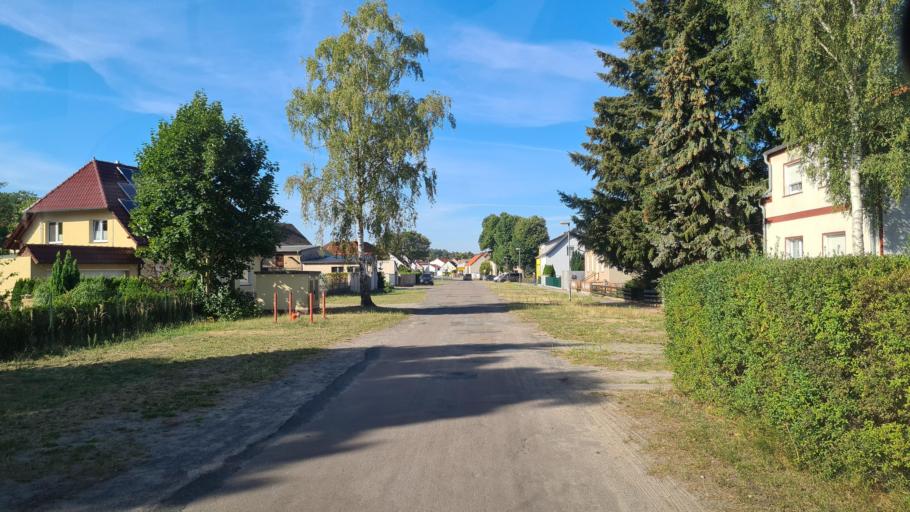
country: DE
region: Brandenburg
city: Golzow
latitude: 52.2805
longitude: 12.6089
